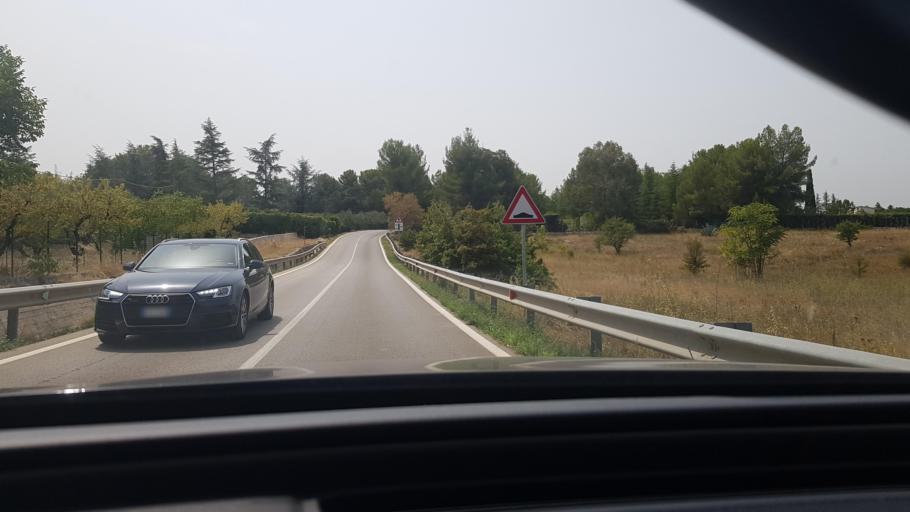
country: IT
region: Apulia
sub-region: Provincia di Barletta - Andria - Trani
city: Andria
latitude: 41.1248
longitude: 16.2872
